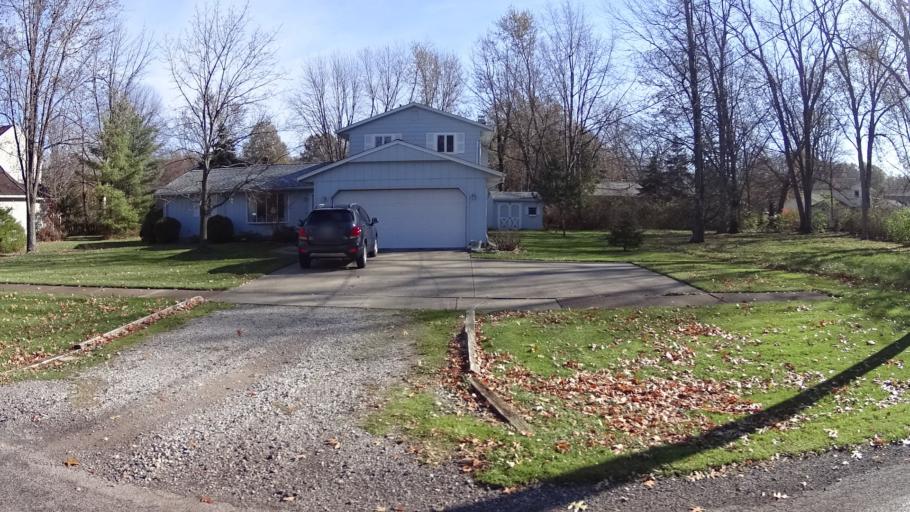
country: US
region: Ohio
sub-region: Lorain County
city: Sheffield Lake
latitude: 41.4949
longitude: -82.0818
